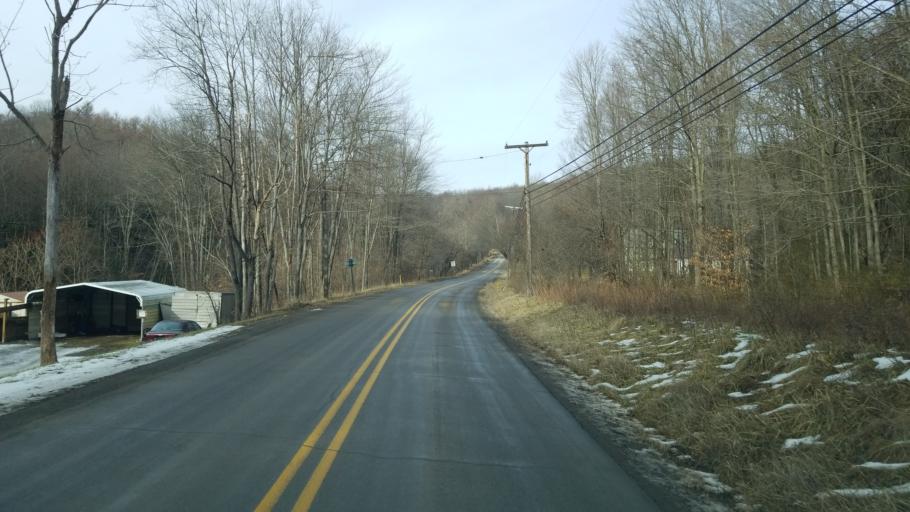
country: US
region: Pennsylvania
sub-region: Indiana County
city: Johnsonburg
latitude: 40.8268
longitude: -78.8350
